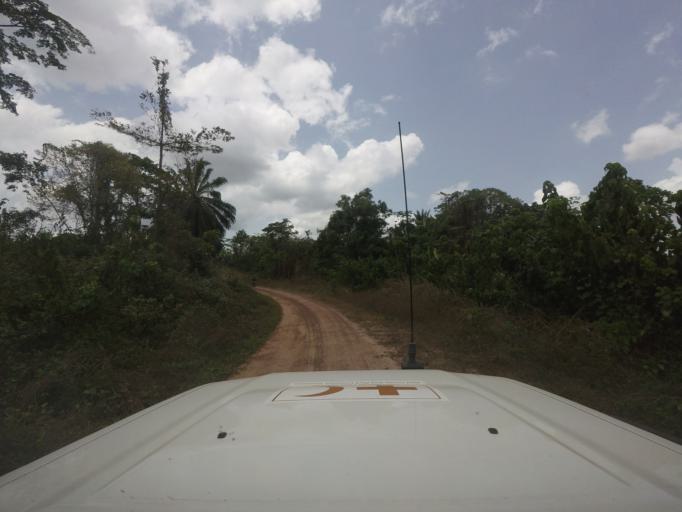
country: GN
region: Nzerekore
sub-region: Yomou
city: Yomou
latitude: 7.2616
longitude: -9.1908
